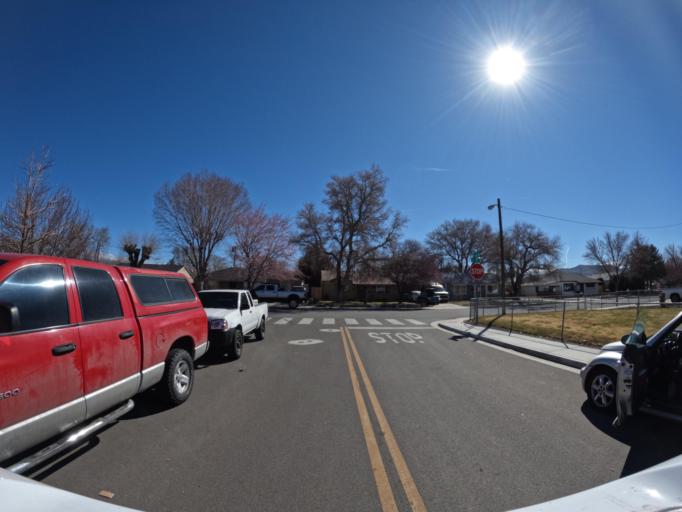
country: US
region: Nevada
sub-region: Washoe County
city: Sparks
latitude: 39.5445
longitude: -119.7446
